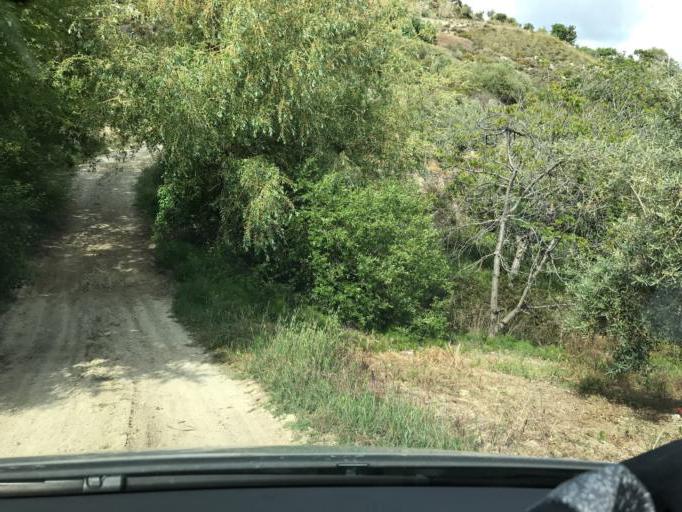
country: ES
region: Andalusia
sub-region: Provincia de Granada
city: Beas de Granada
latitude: 37.2196
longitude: -3.4544
